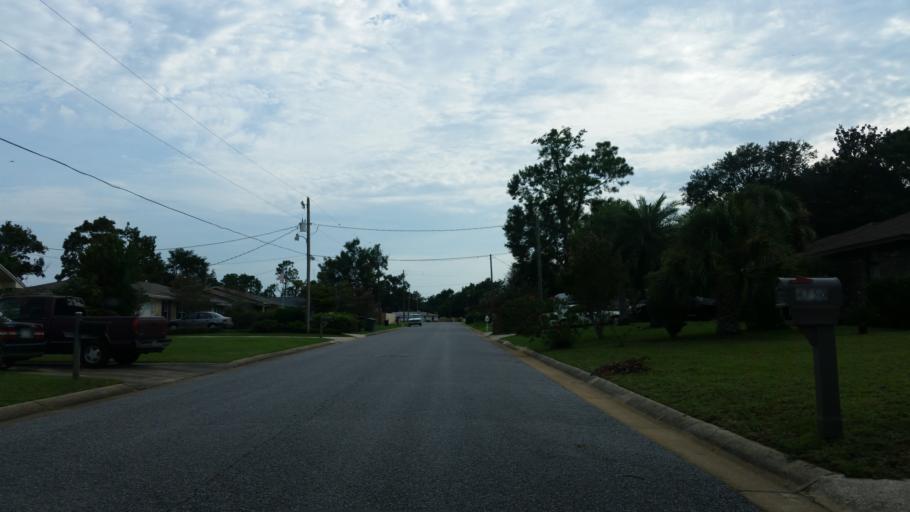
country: US
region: Florida
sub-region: Escambia County
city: Ferry Pass
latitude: 30.5144
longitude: -87.1739
